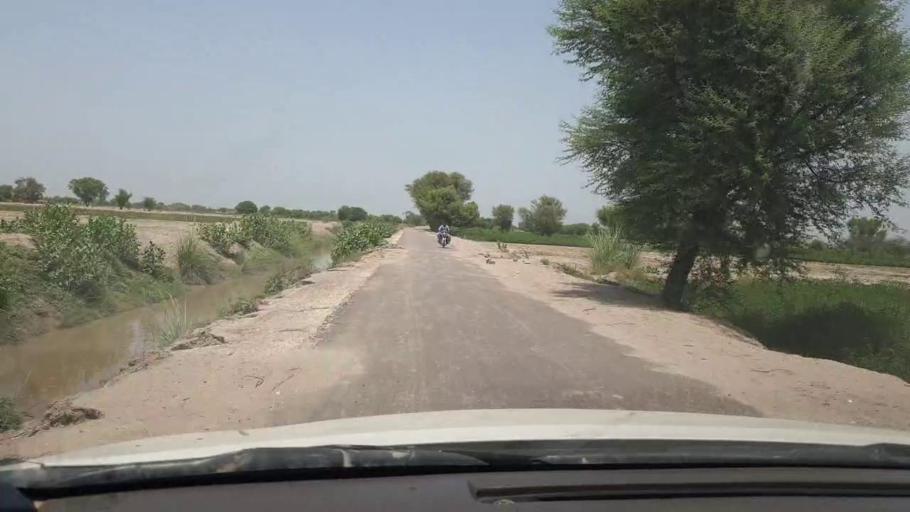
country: PK
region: Sindh
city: Rohri
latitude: 27.5190
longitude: 69.1784
